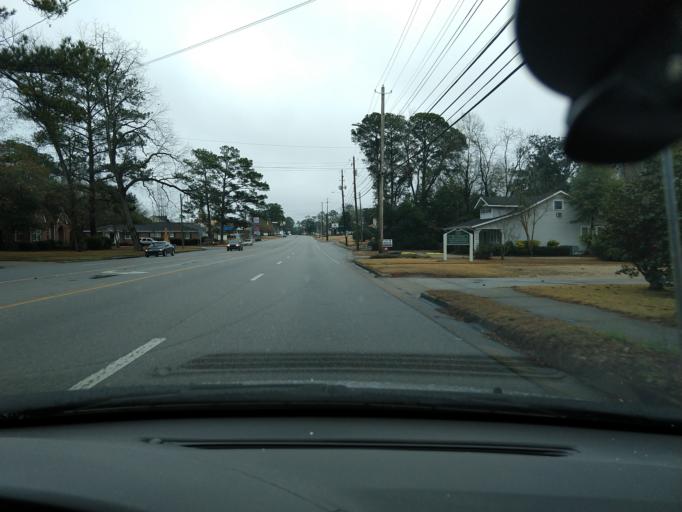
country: US
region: Alabama
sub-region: Houston County
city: Dothan
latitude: 31.2275
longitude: -85.4143
